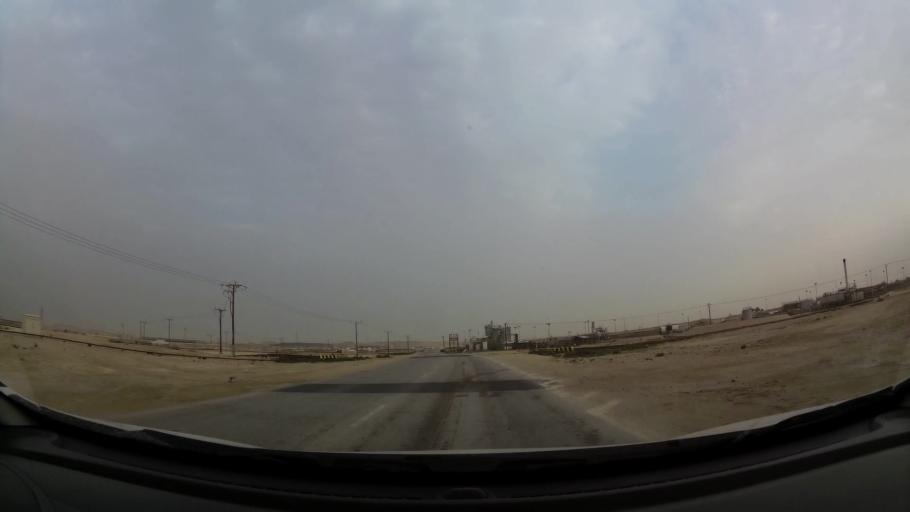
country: BH
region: Central Governorate
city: Dar Kulayb
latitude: 26.0184
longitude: 50.5738
